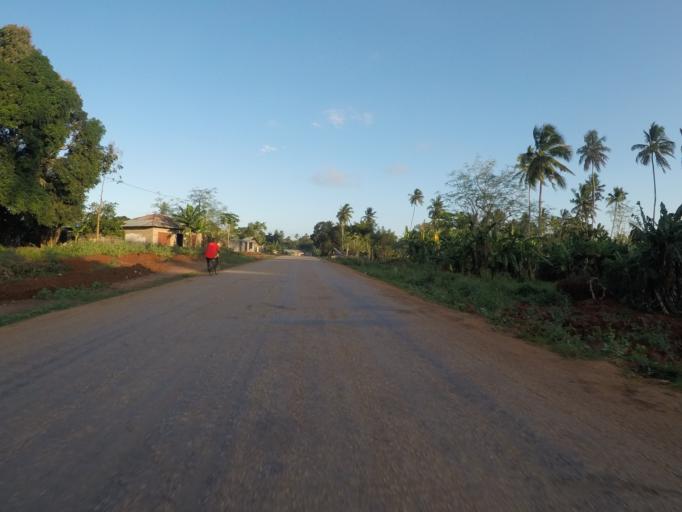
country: TZ
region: Zanzibar North
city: Gamba
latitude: -5.8976
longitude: 39.2934
